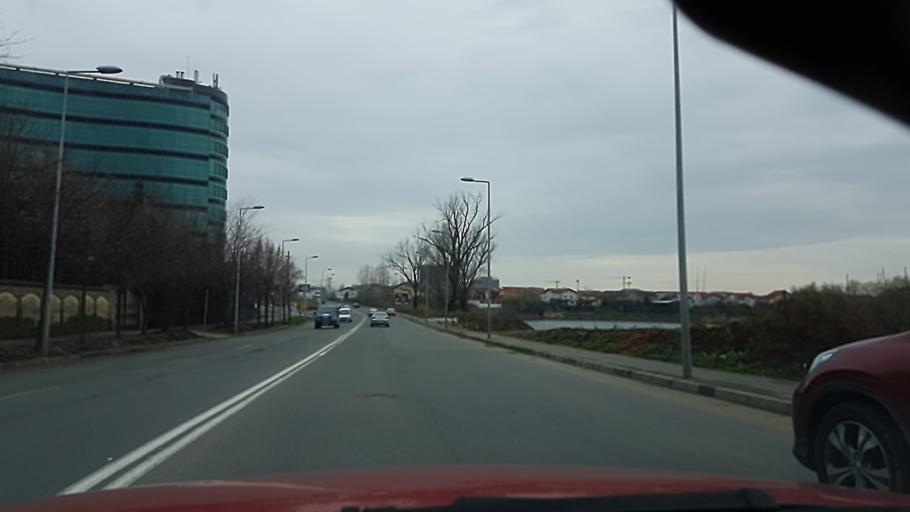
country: RO
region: Ilfov
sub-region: Voluntari City
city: Voluntari
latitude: 44.4987
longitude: 26.1339
